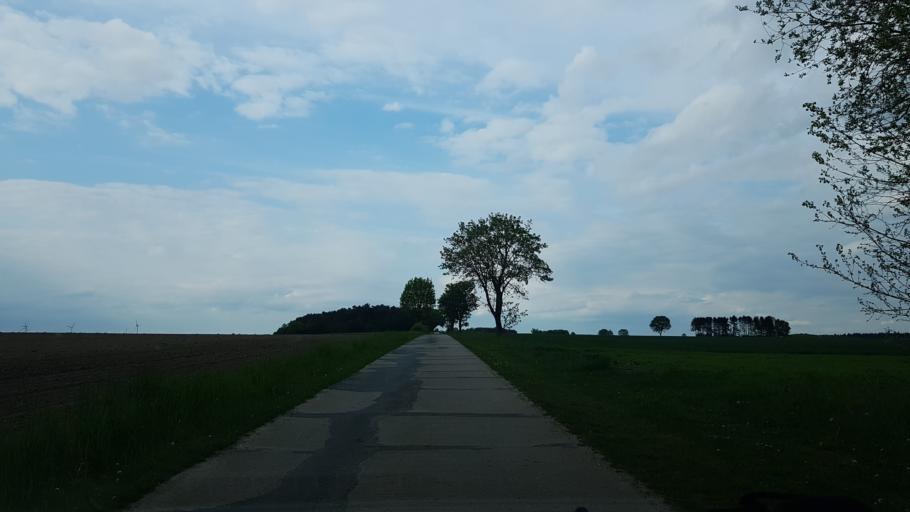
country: DE
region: Lower Saxony
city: Vastorf
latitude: 53.1754
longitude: 10.5506
